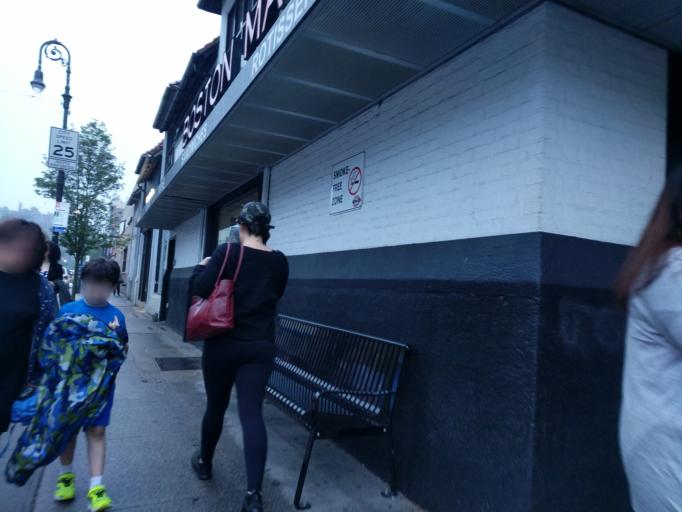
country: US
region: New York
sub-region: Queens County
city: Borough of Queens
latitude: 40.7201
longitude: -73.8448
